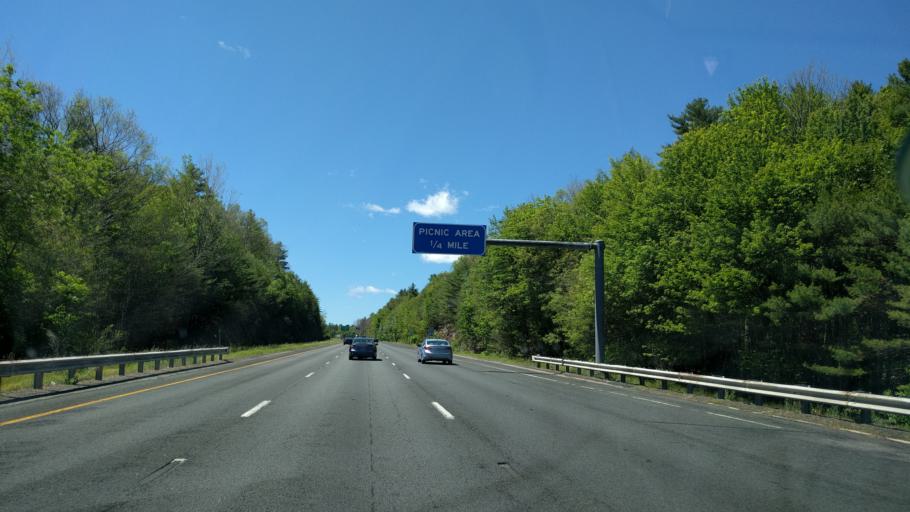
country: US
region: Massachusetts
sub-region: Worcester County
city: Sturbridge
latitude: 42.0886
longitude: -72.0933
